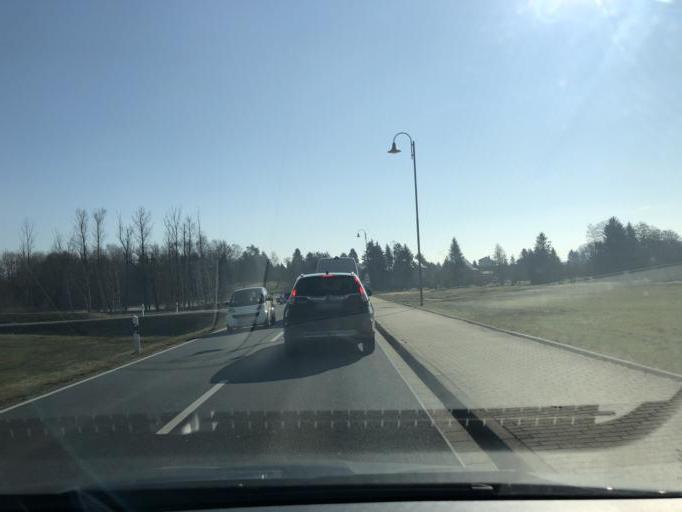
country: DE
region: Saxony
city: Rammenau
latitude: 51.1533
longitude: 14.1438
